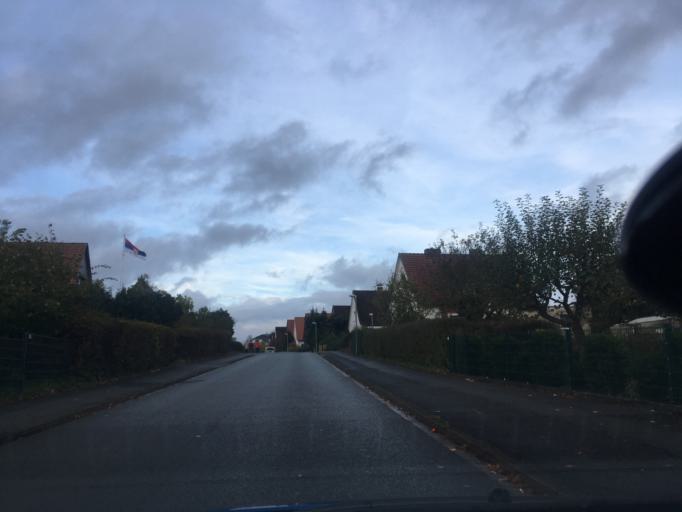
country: DE
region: Lower Saxony
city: Lueneburg
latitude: 53.2420
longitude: 10.4411
